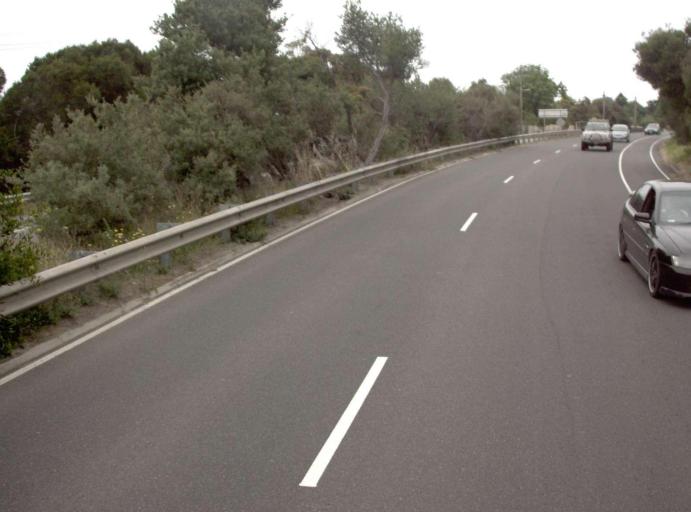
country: AU
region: Victoria
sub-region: Mornington Peninsula
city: Mount Eliza
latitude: -38.1654
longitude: 145.1017
